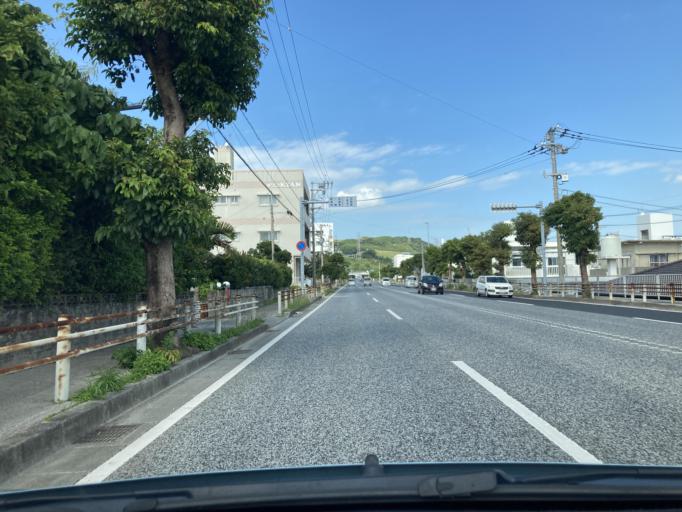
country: JP
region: Okinawa
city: Ginowan
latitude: 26.2653
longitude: 127.7900
